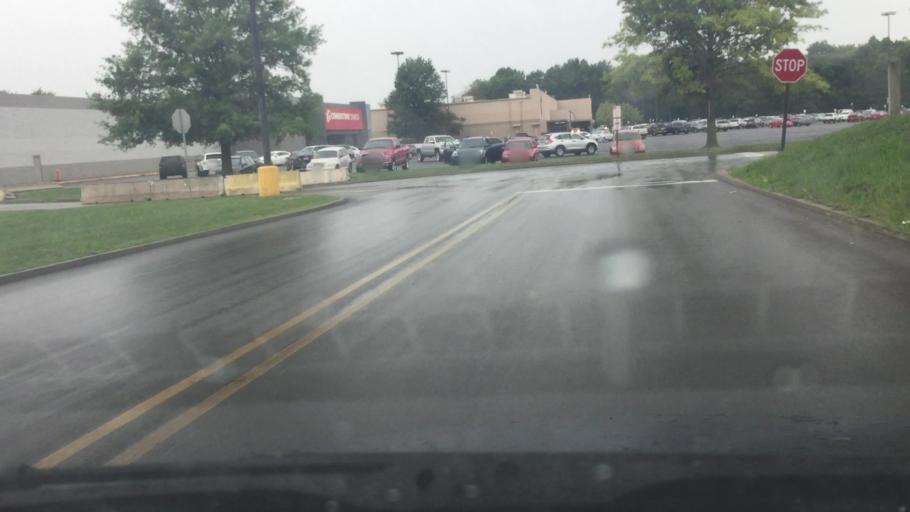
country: US
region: Illinois
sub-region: Williamson County
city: Marion
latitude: 37.7397
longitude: -88.9664
